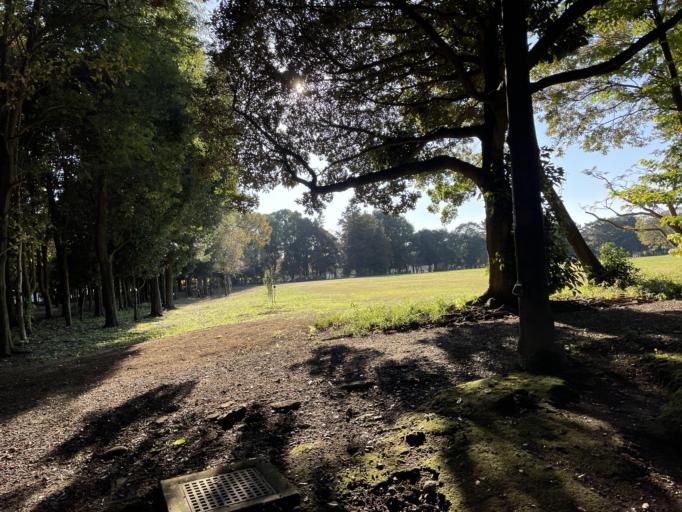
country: JP
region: Gunma
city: Tatebayashi
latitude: 36.2431
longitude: 139.5458
